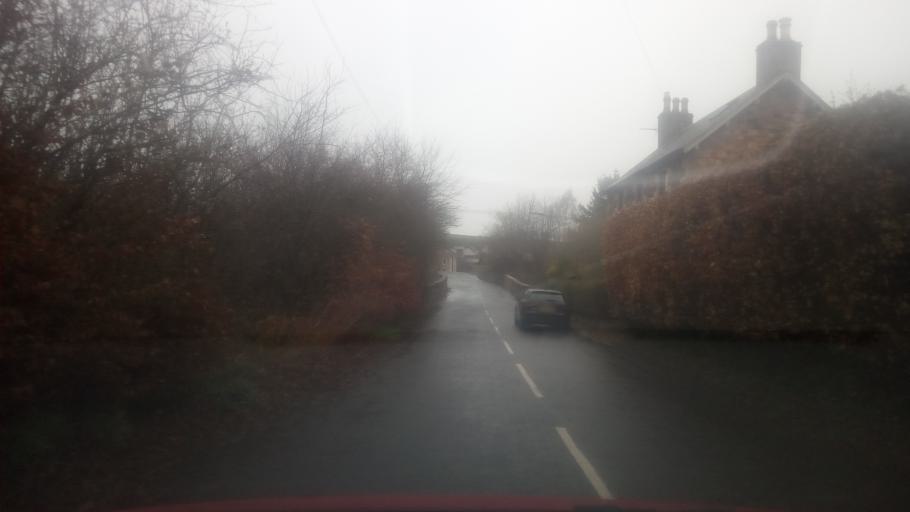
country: GB
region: Scotland
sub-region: The Scottish Borders
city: Earlston
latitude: 55.6355
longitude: -2.6752
